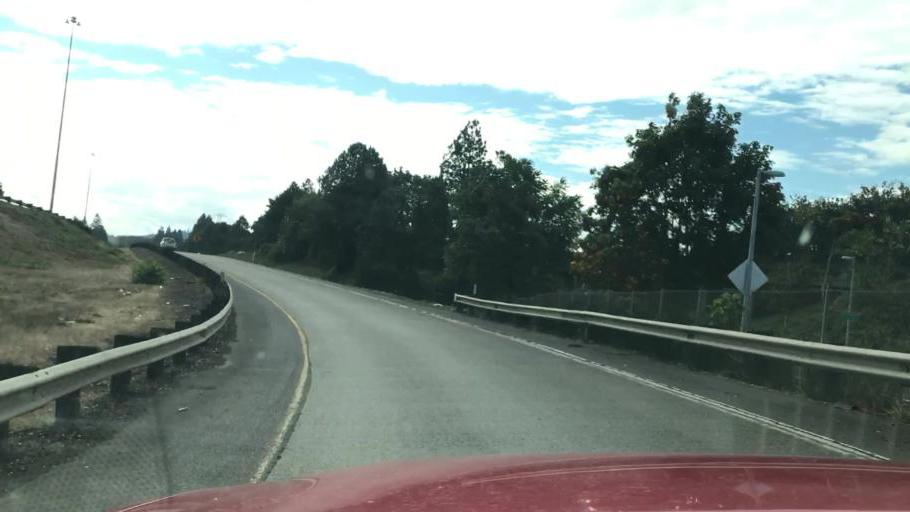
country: US
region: Oregon
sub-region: Lane County
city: Springfield
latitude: 44.0623
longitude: -123.0519
